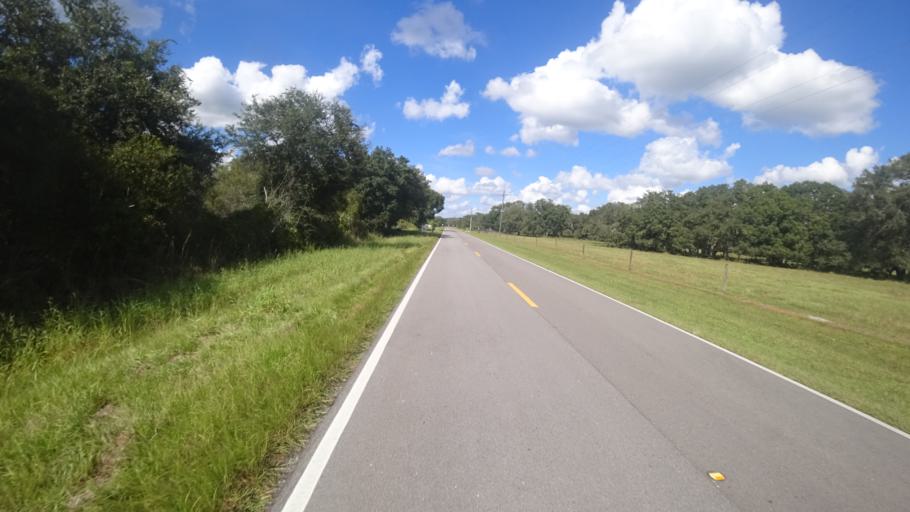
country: US
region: Florida
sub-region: Sarasota County
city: Lake Sarasota
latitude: 27.2850
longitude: -82.2153
